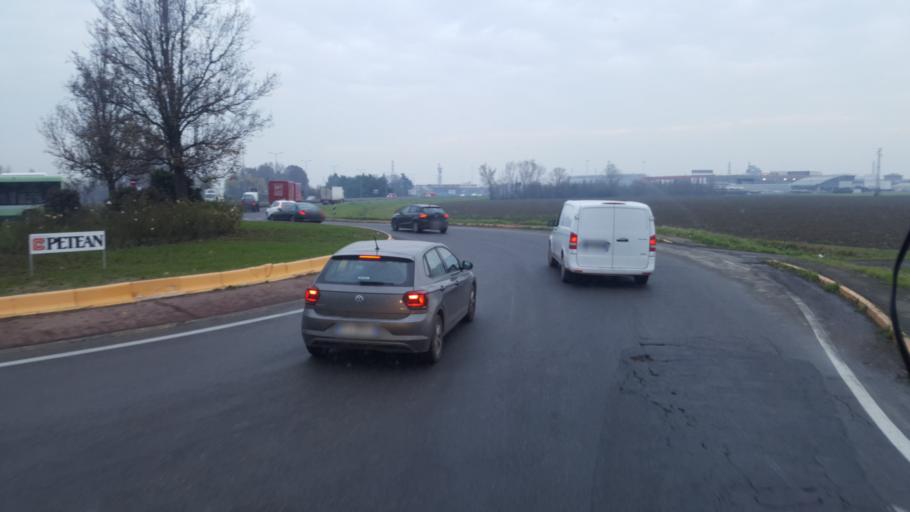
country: IT
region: Emilia-Romagna
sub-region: Provincia di Parma
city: Parma
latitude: 44.8318
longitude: 10.3307
